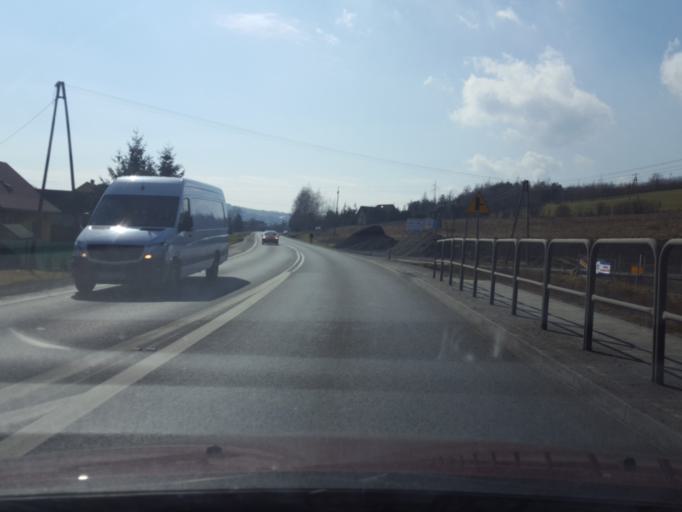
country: PL
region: Lesser Poland Voivodeship
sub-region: Powiat nowosadecki
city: Lososina Dolna
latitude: 49.7641
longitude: 20.6325
